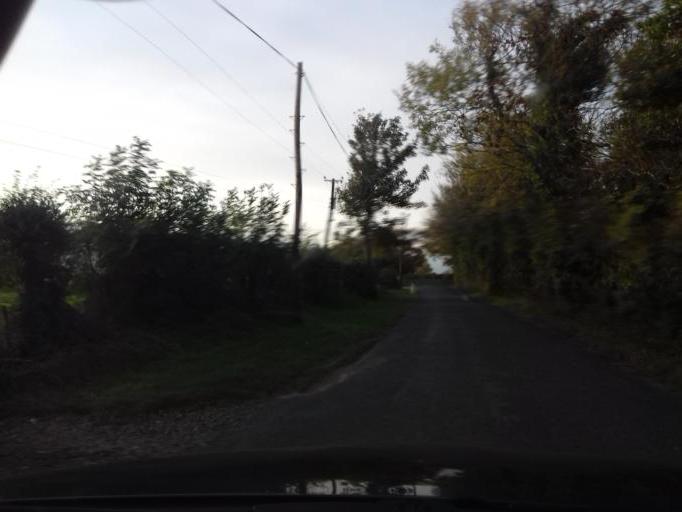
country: IE
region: Leinster
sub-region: An Mhi
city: Dunboyne
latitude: 53.3876
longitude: -6.4658
